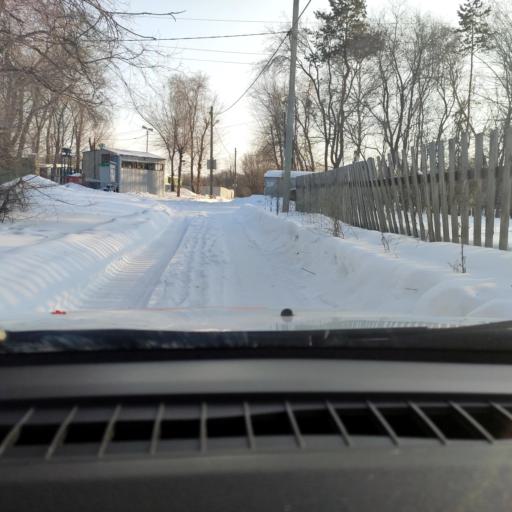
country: RU
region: Samara
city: Samara
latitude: 53.1294
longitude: 50.2597
